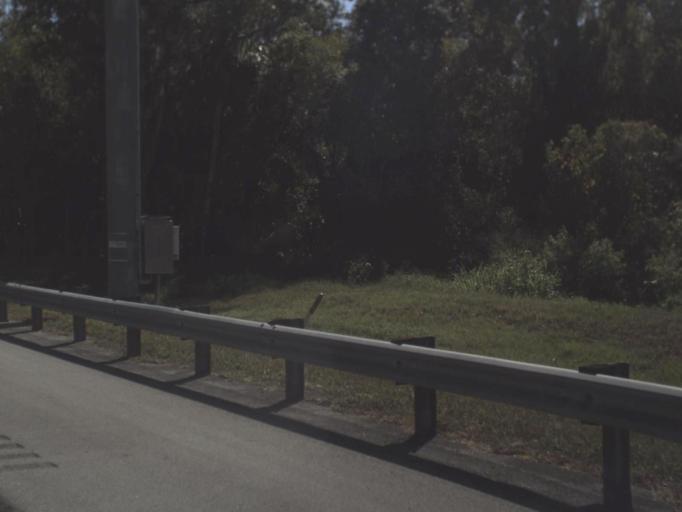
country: US
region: Florida
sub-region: Seminole County
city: Oviedo
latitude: 28.6985
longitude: -81.2319
